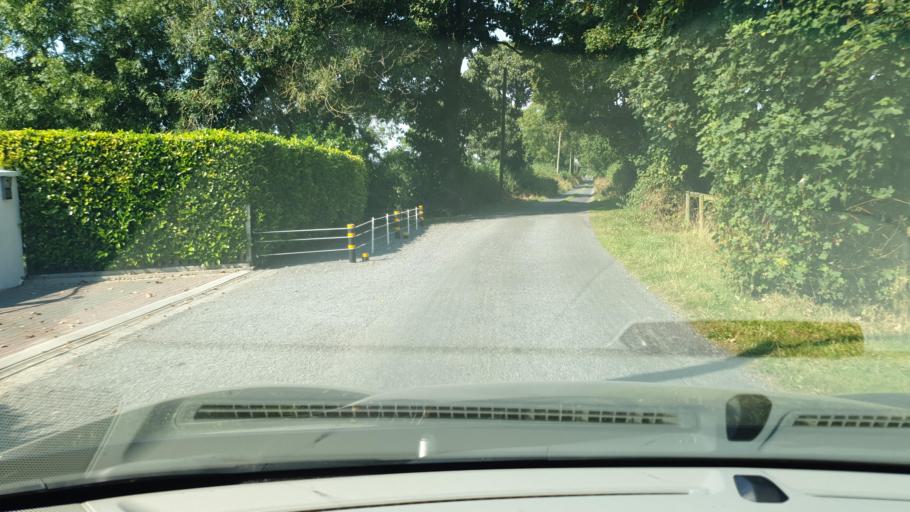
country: IE
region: Leinster
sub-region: An Mhi
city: Athboy
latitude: 53.6180
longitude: -6.9925
